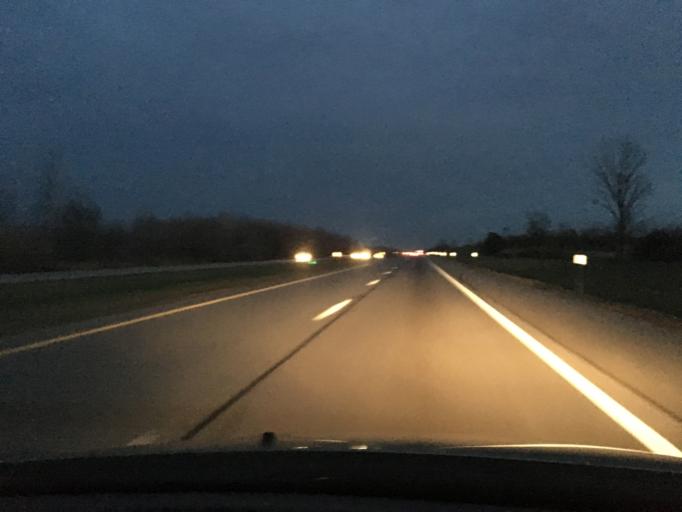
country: US
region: New York
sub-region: Wayne County
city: Macedon
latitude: 42.9903
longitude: -77.3234
